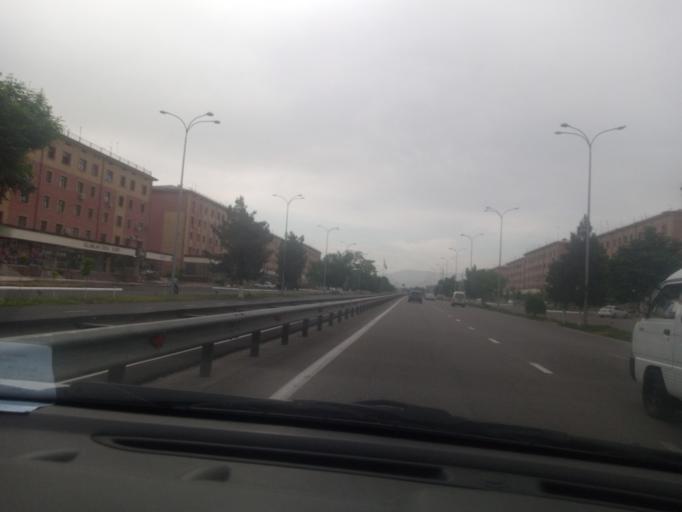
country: UZ
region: Toshkent
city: Ohangaron
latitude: 40.9076
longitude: 69.6285
